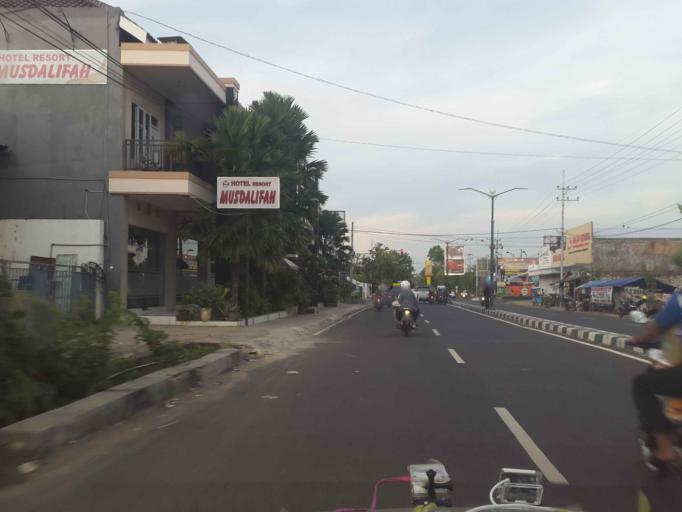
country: ID
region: East Java
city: Sumenep
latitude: -7.0277
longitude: 113.8538
